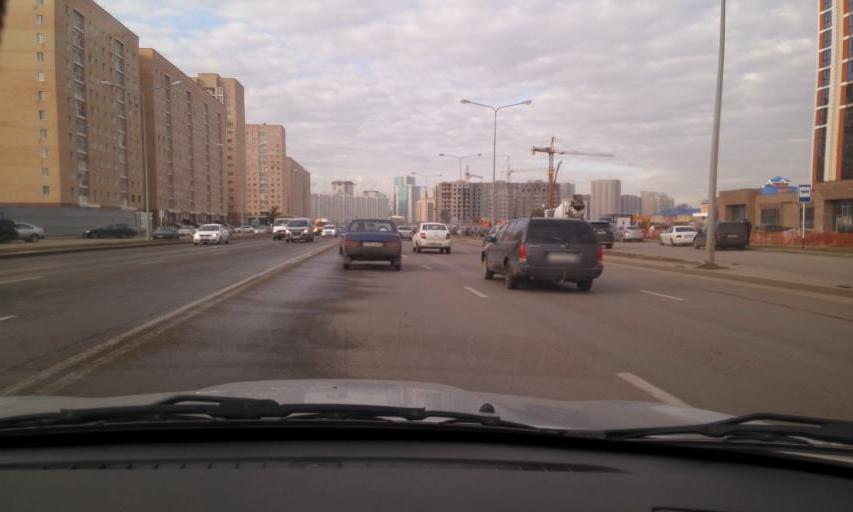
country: KZ
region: Astana Qalasy
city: Astana
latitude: 51.1287
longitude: 71.4959
